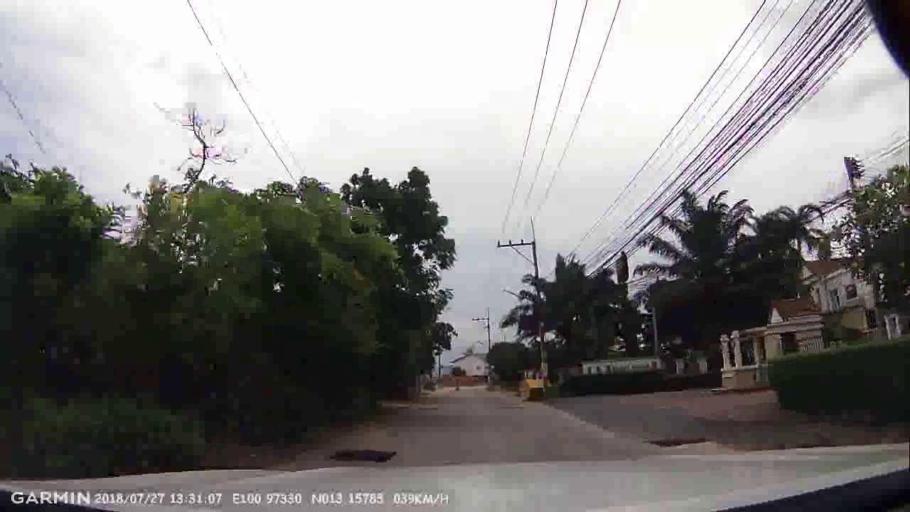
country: TH
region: Chon Buri
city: Si Racha
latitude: 13.1580
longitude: 100.9733
